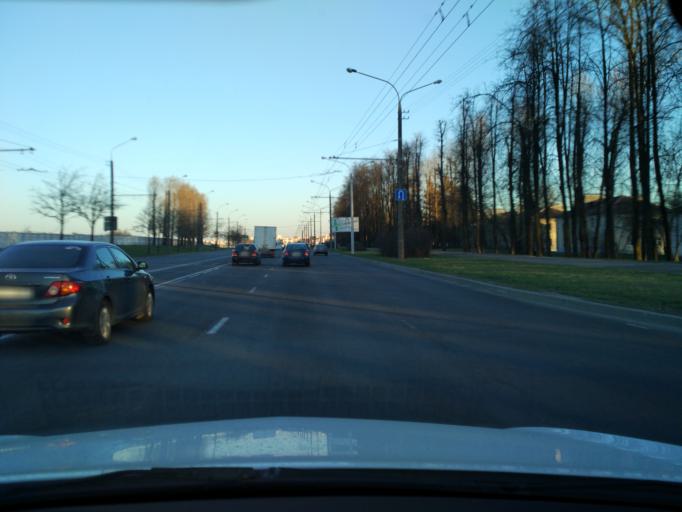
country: BY
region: Minsk
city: Syenitsa
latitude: 53.8646
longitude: 27.5307
